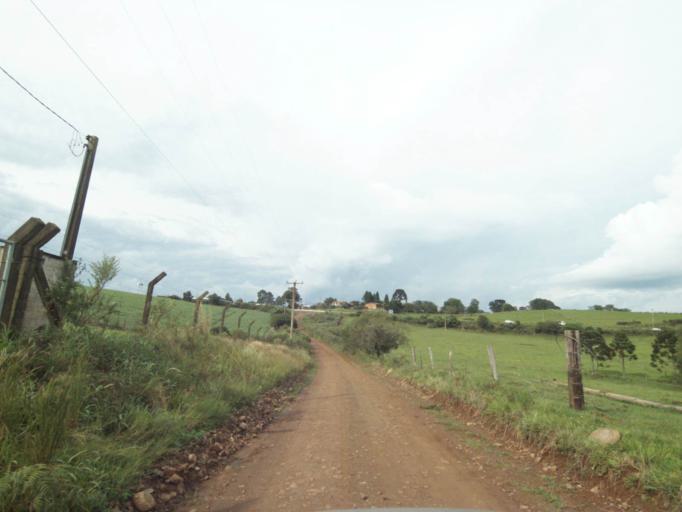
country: BR
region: Rio Grande do Sul
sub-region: Lagoa Vermelha
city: Lagoa Vermelha
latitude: -28.2275
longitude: -51.5041
